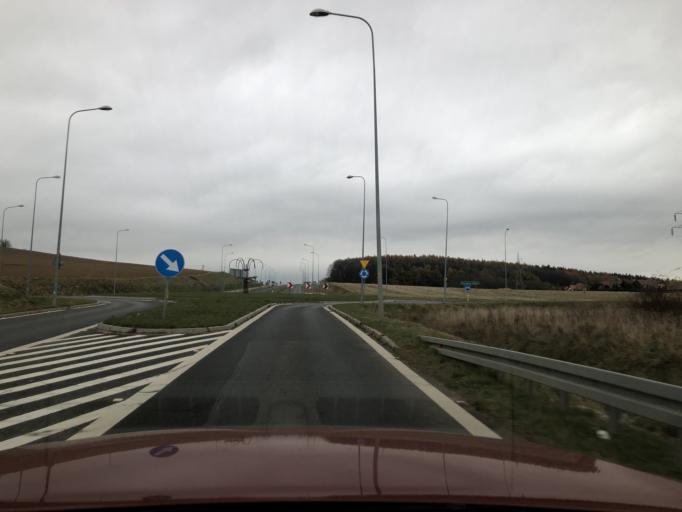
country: PL
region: Lower Silesian Voivodeship
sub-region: Powiat walbrzyski
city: Szczawno-Zdroj
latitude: 50.8112
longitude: 16.2306
